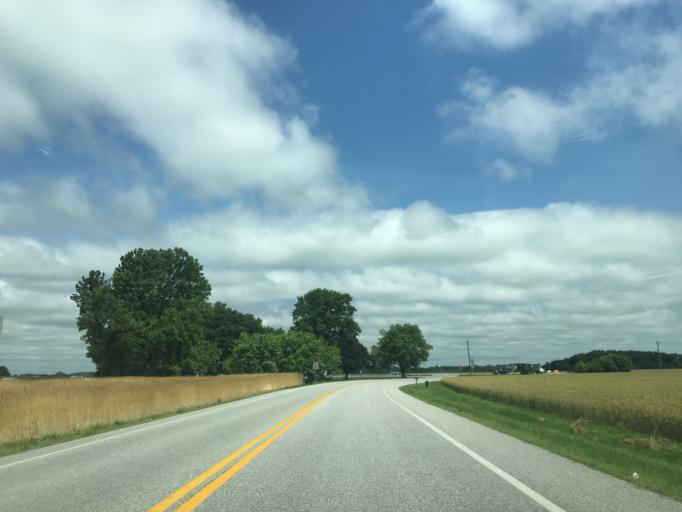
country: US
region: Maryland
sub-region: Caroline County
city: Ridgely
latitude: 38.9336
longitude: -75.8945
